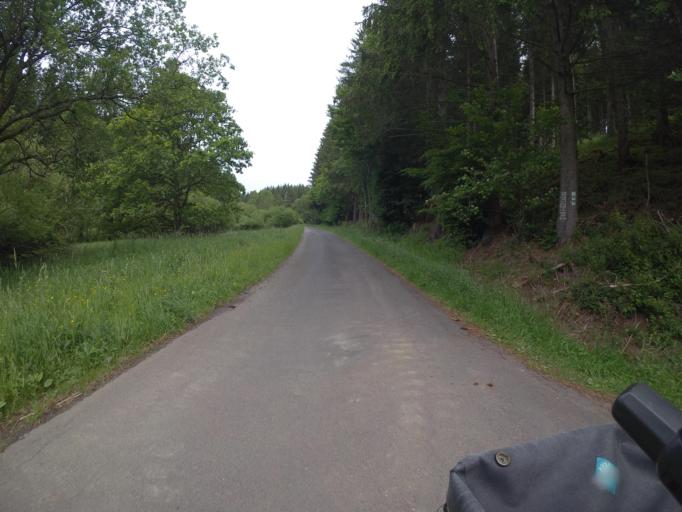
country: DE
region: Rheinland-Pfalz
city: Scheid
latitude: 50.3984
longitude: 6.3905
